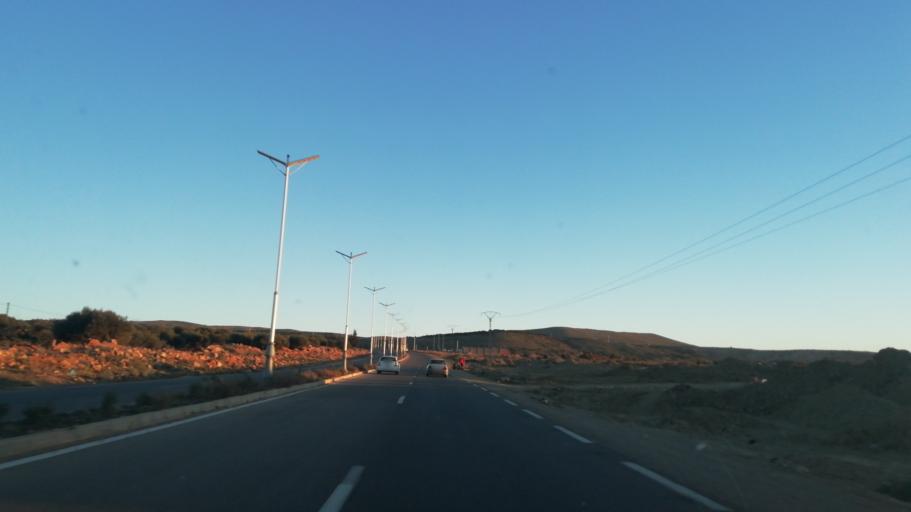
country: DZ
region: Saida
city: Saida
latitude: 34.8620
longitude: 0.1943
